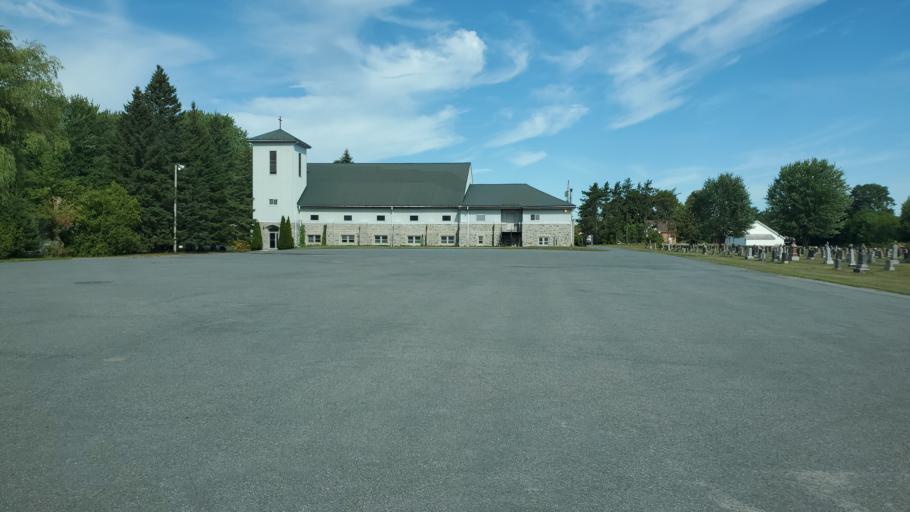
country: CA
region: Ontario
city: Cornwall
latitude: 45.2194
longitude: -74.7681
